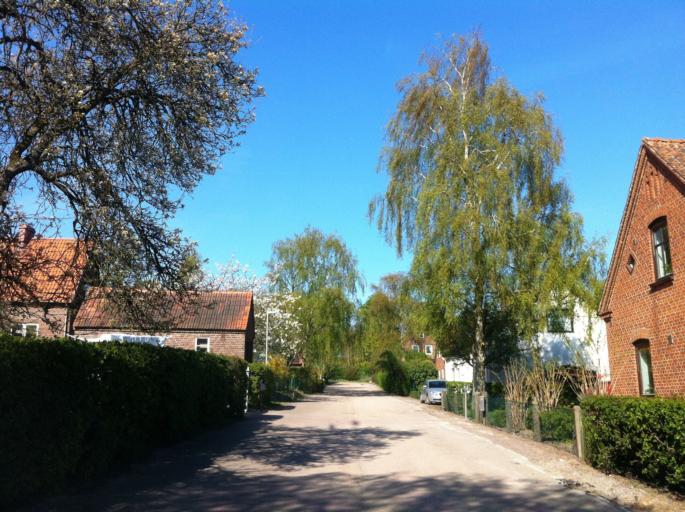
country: SE
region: Skane
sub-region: Svalovs Kommun
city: Kagerod
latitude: 55.9709
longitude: 13.0567
